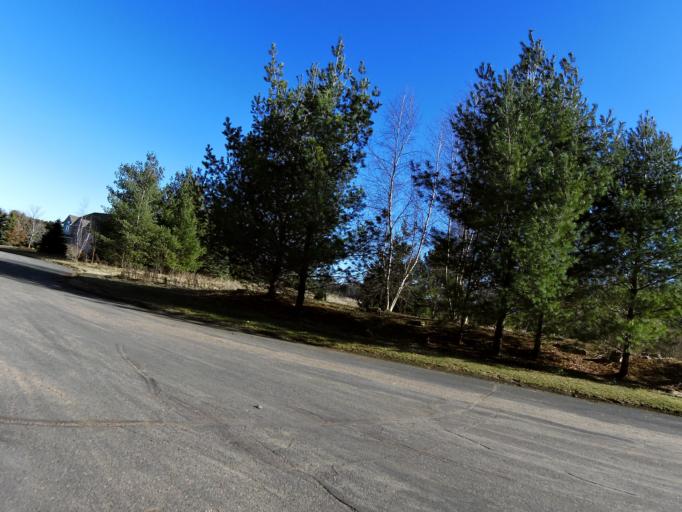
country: US
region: Minnesota
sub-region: Washington County
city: Oak Park Heights
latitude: 44.9899
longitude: -92.8261
